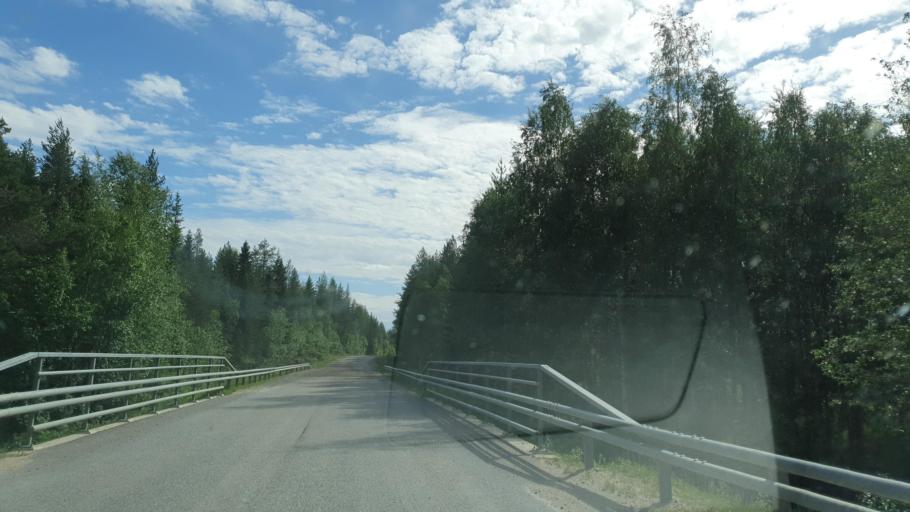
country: FI
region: Kainuu
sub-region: Kehys-Kainuu
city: Kuhmo
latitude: 64.4662
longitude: 29.5385
